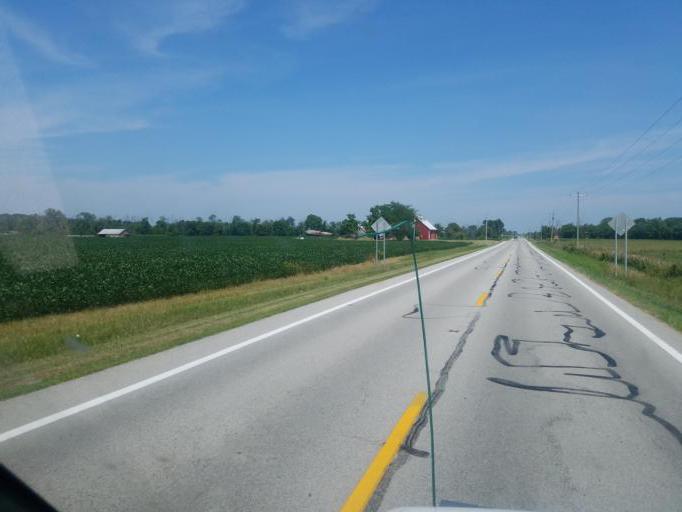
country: US
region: Ohio
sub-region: Auglaize County
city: Saint Marys
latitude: 40.4952
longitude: -84.3749
